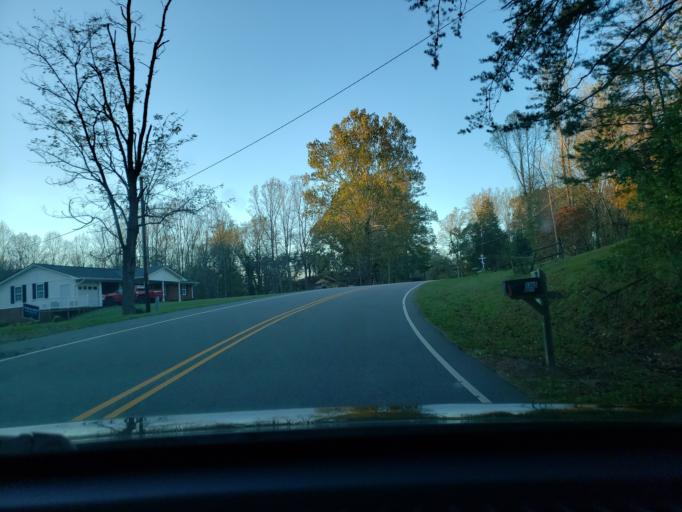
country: US
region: North Carolina
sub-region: Stokes County
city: Danbury
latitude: 36.3966
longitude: -80.1990
